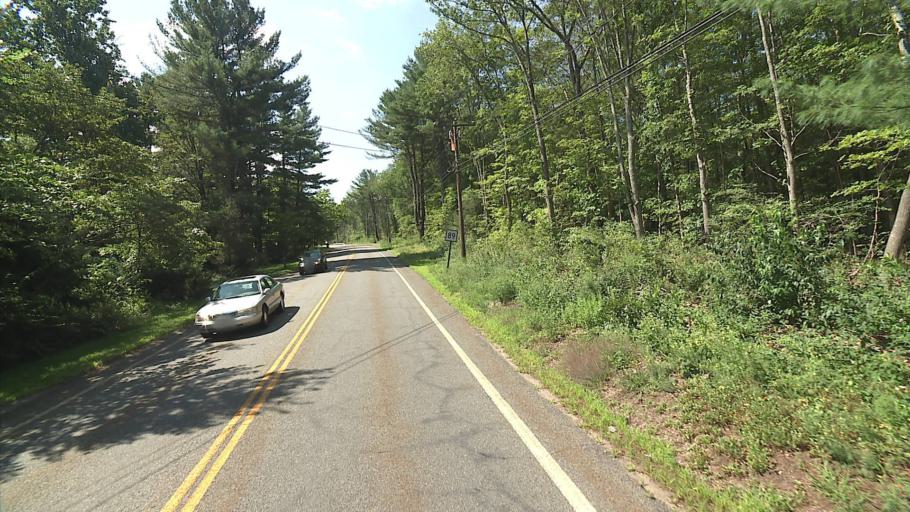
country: US
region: Connecticut
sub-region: Tolland County
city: Mansfield City
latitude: 41.7707
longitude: -72.1955
